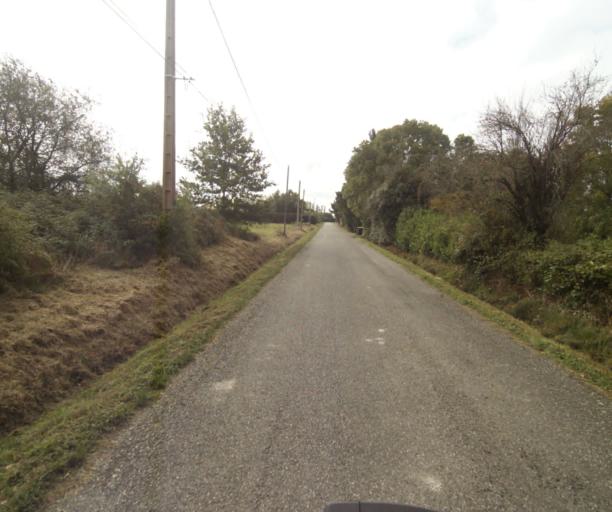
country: FR
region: Midi-Pyrenees
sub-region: Departement du Tarn-et-Garonne
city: Finhan
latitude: 43.9239
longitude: 1.2457
